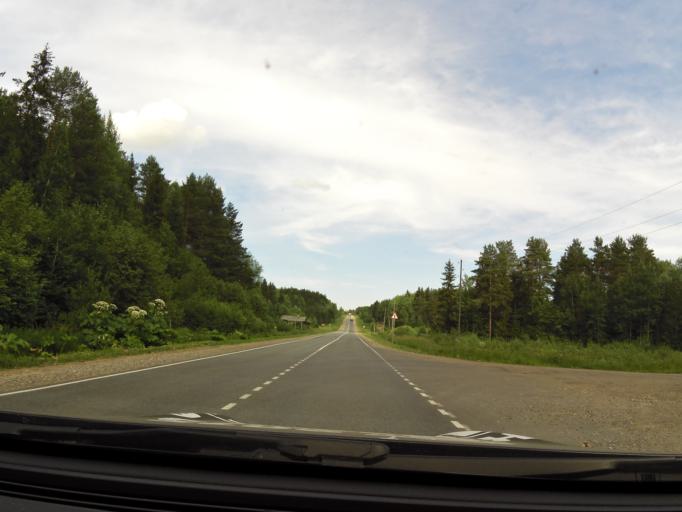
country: RU
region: Kirov
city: Slobodskoy
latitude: 58.7310
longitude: 50.2698
